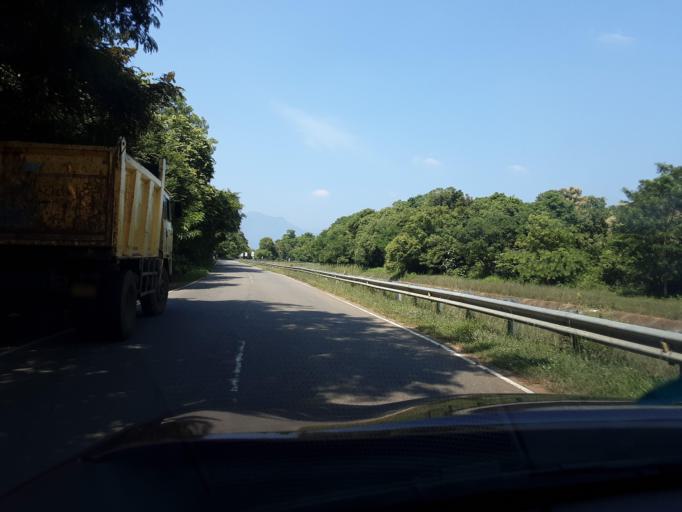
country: LK
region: Uva
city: Badulla
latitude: 7.2735
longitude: 81.0485
